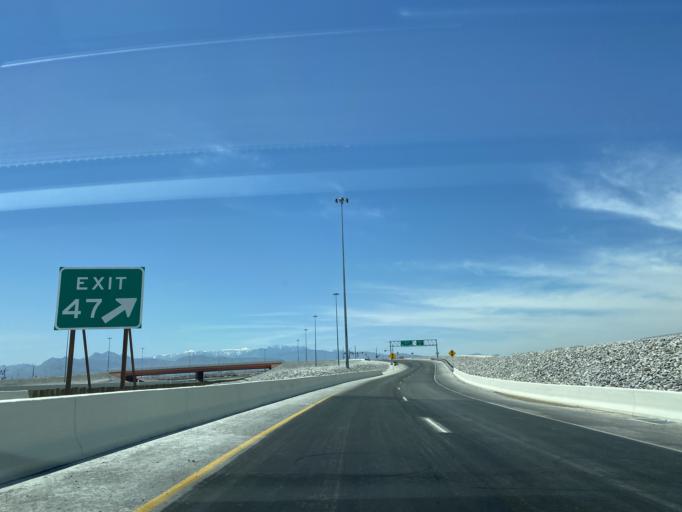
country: US
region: Nevada
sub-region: Clark County
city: Nellis Air Force Base
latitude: 36.2898
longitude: -115.1128
